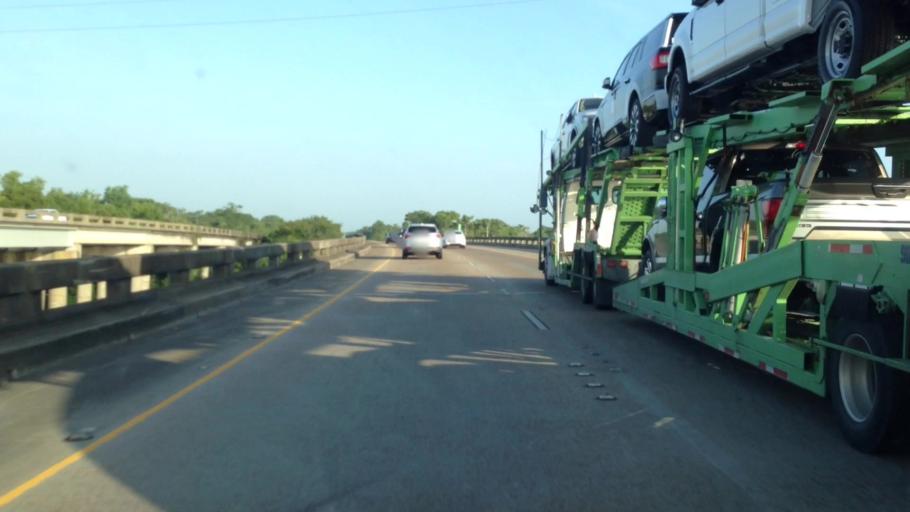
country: US
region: Louisiana
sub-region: Saint John the Baptist Parish
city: Laplace
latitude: 30.0781
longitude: -90.4049
